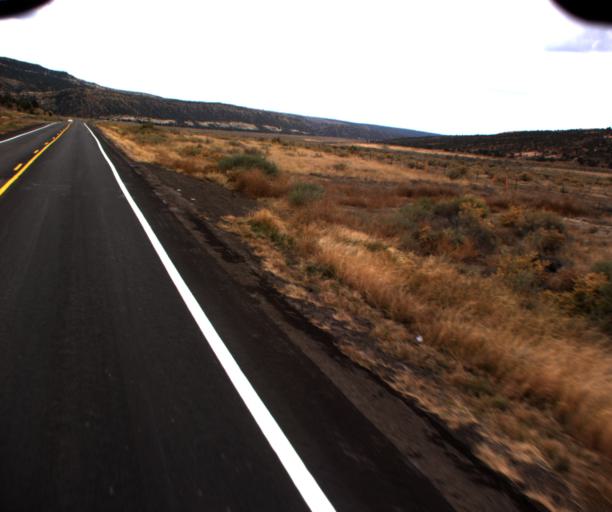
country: US
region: Arizona
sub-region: Navajo County
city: Kayenta
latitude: 36.5964
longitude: -110.4724
